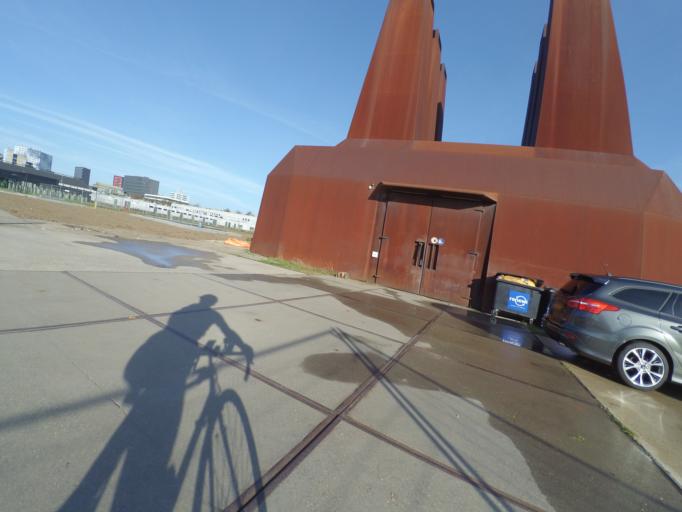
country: NL
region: Utrecht
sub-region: Gemeente Bunnik
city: Bunnik
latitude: 52.0813
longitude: 5.1847
